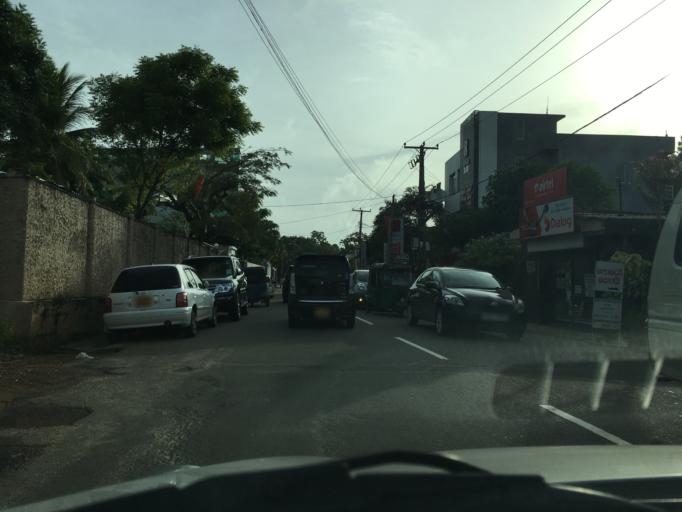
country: LK
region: Western
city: Sri Jayewardenepura Kotte
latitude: 6.8840
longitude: 79.9011
